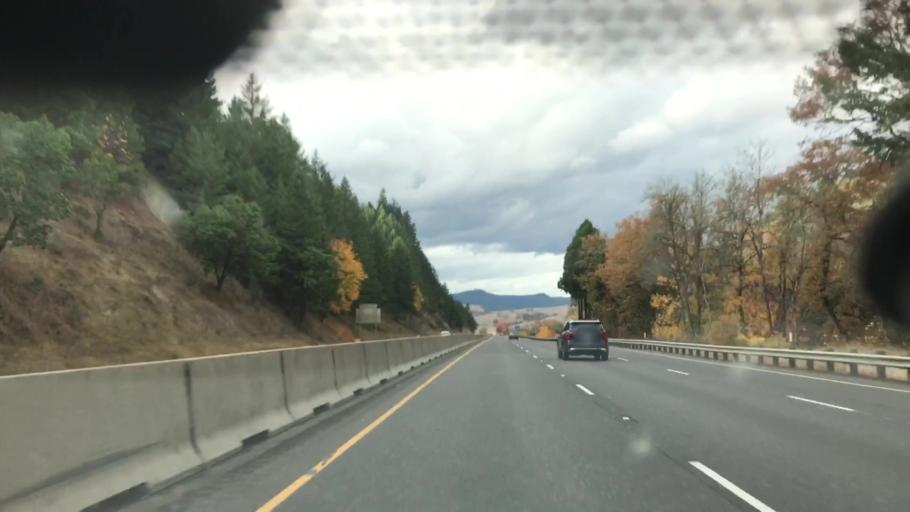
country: US
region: Oregon
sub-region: Douglas County
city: Sutherlin
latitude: 43.4393
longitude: -123.3155
